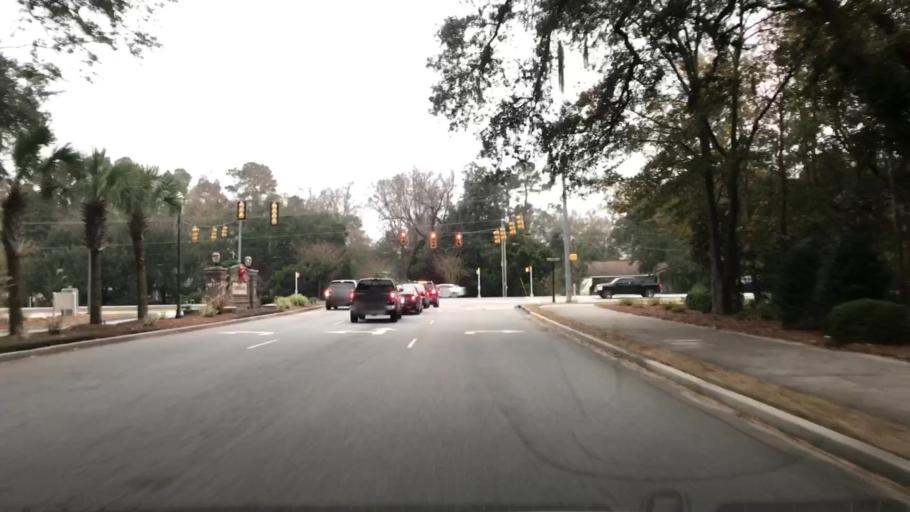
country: US
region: South Carolina
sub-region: Charleston County
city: Shell Point
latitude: 32.7973
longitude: -80.0812
